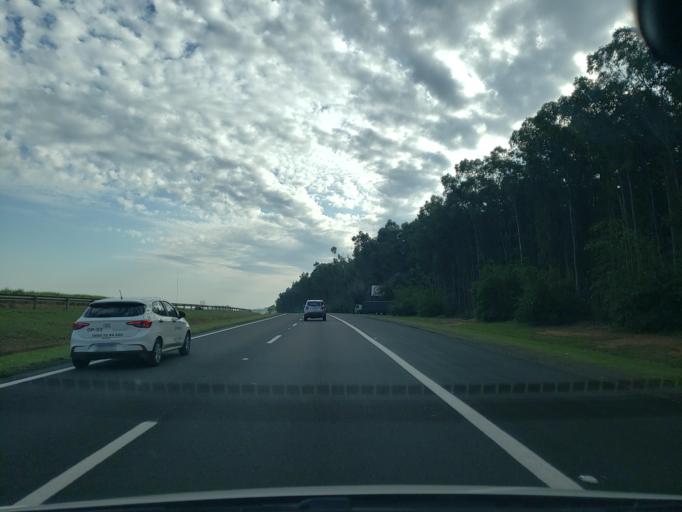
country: BR
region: Sao Paulo
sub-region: Guararapes
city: Guararapes
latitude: -21.1997
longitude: -50.5663
